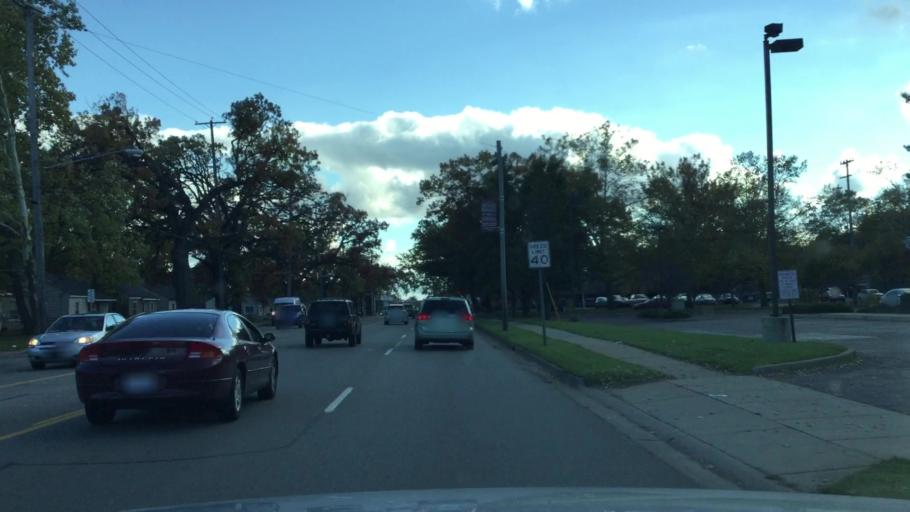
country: US
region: Michigan
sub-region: Kalamazoo County
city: Kalamazoo
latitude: 42.2504
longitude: -85.5897
